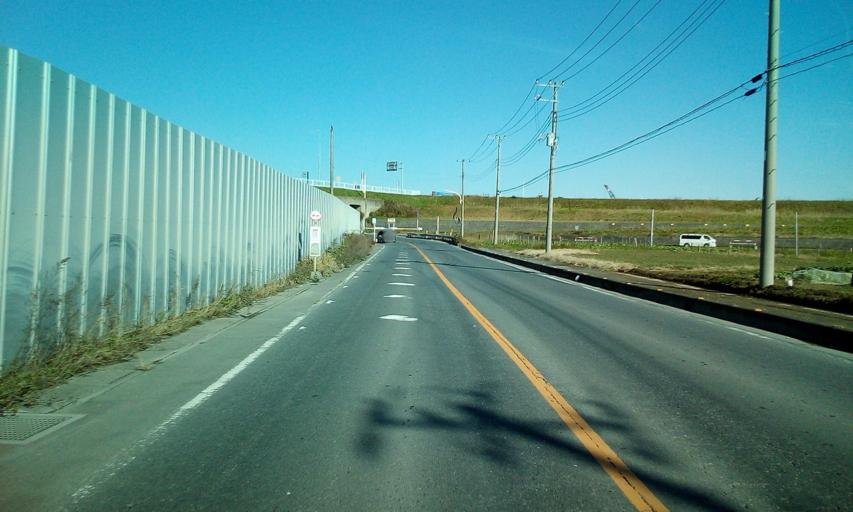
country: JP
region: Chiba
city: Noda
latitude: 35.9113
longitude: 139.8696
